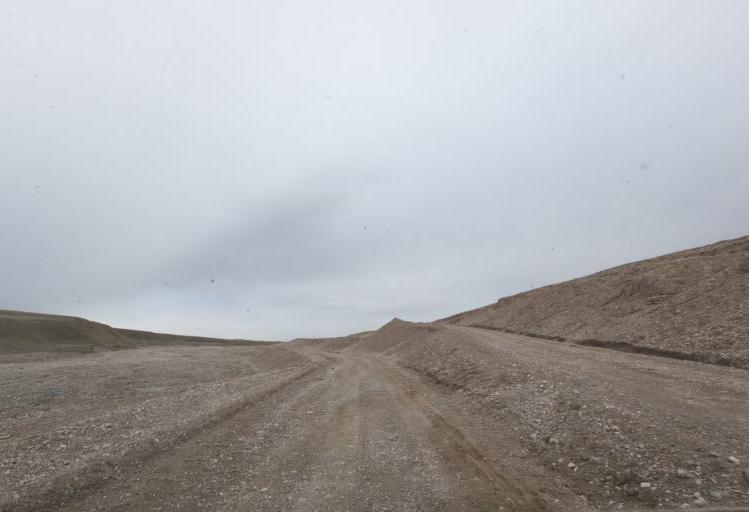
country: KG
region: Naryn
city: Baetov
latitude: 40.9371
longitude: 75.2788
